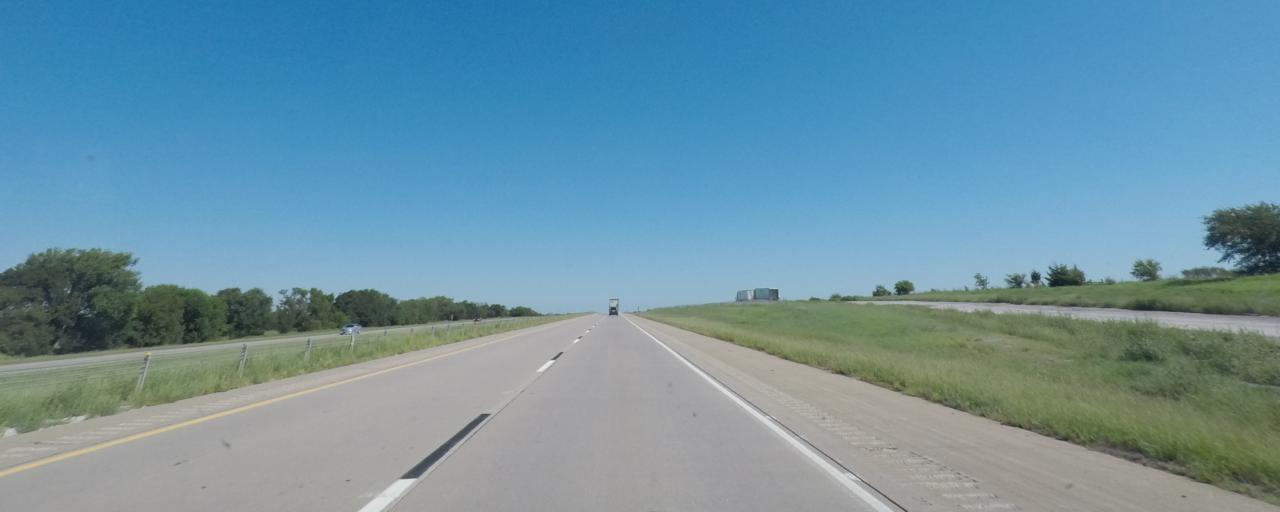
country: US
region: Oklahoma
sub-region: Noble County
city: Perry
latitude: 36.4248
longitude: -97.3268
